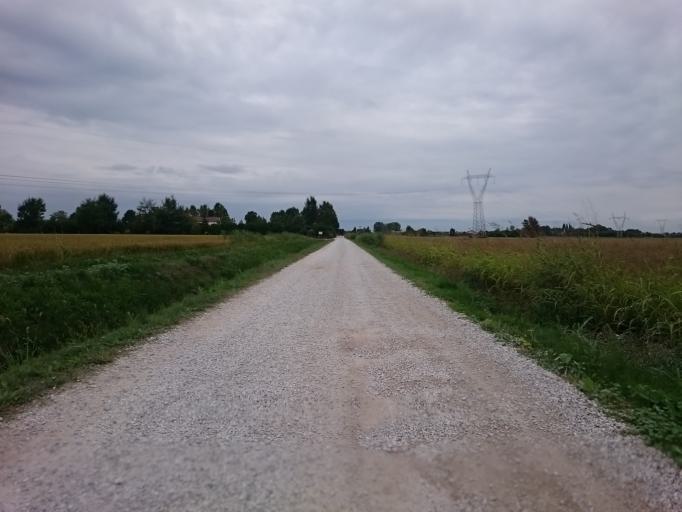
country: IT
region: Veneto
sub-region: Provincia di Vicenza
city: Grumolo delle Abbadesse
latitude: 45.5007
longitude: 11.6582
